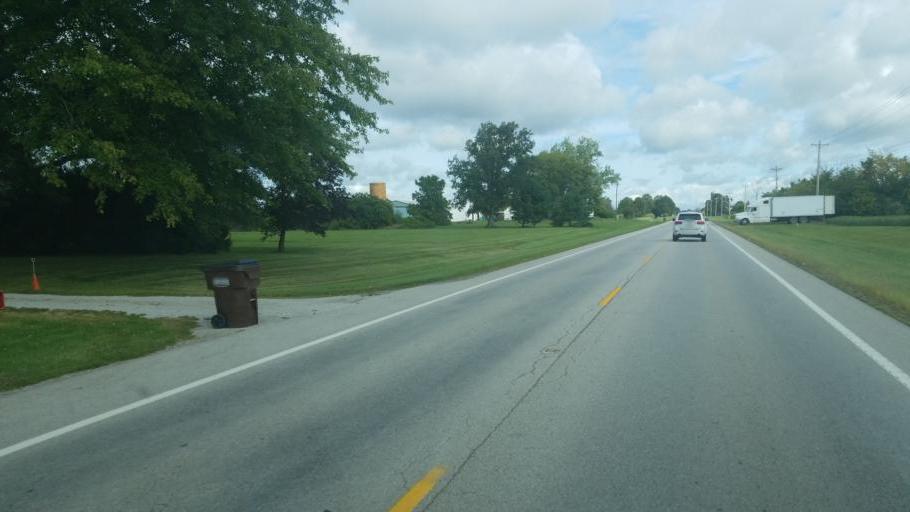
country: US
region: Ohio
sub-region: Lorain County
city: Oberlin
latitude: 41.2450
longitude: -82.2180
